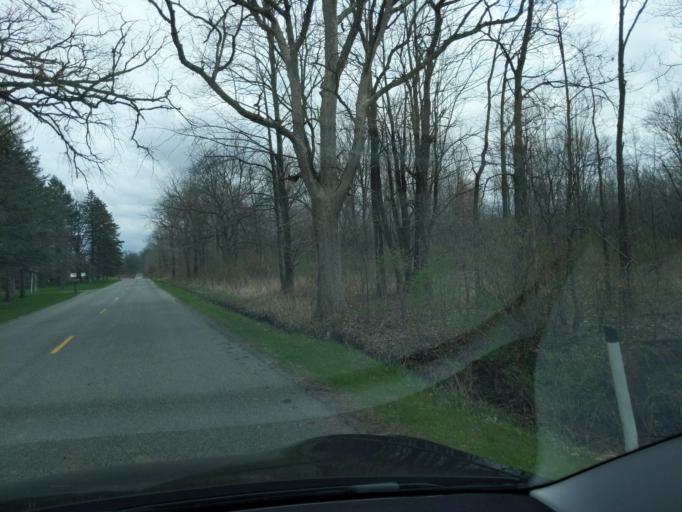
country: US
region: Michigan
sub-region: Ingham County
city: Holt
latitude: 42.5676
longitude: -84.5723
